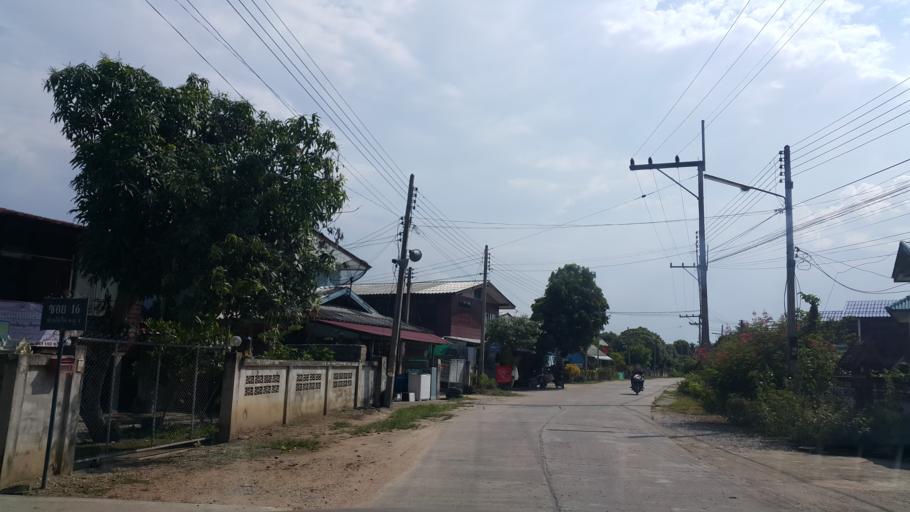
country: TH
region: Chiang Rai
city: Wiang Chai
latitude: 19.9360
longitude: 99.9368
